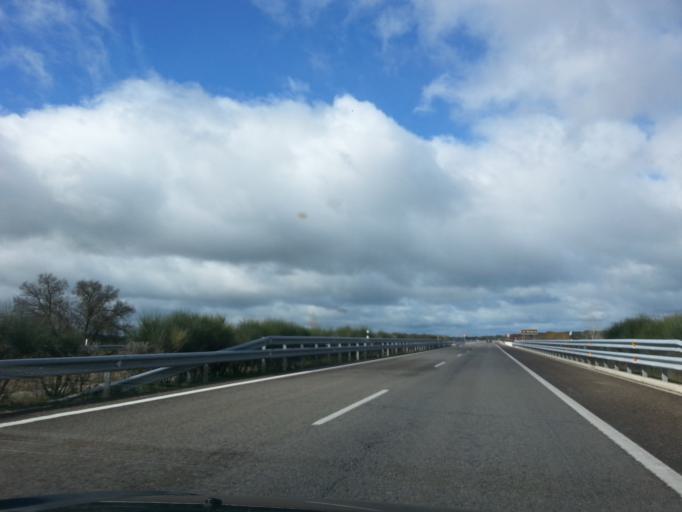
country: ES
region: Castille and Leon
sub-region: Provincia de Salamanca
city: San Munoz
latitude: 40.8090
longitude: -6.1559
